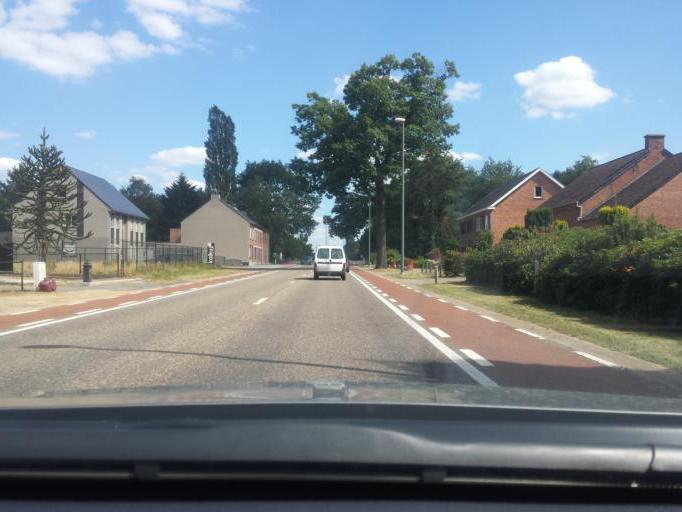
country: BE
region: Flanders
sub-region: Provincie Limburg
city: Heusden
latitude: 51.0285
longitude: 5.2619
